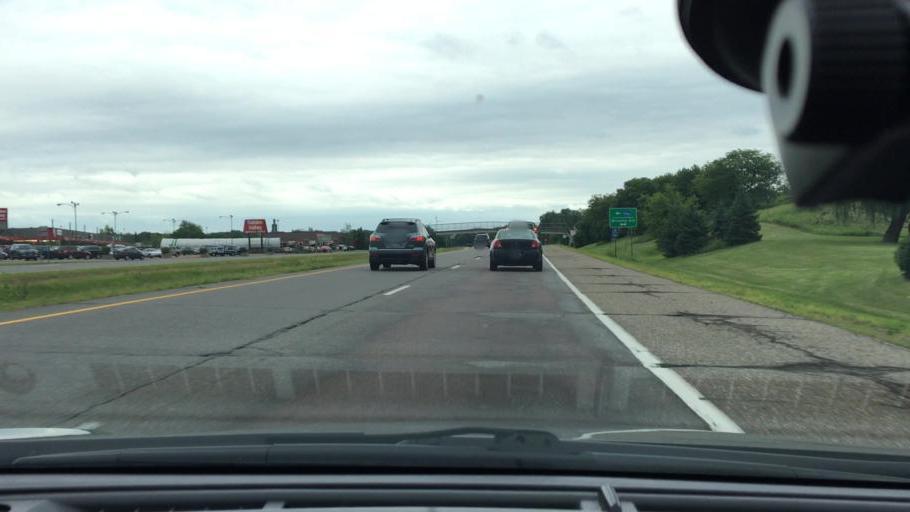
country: US
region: Minnesota
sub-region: Hennepin County
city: Golden Valley
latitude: 44.9844
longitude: -93.3847
